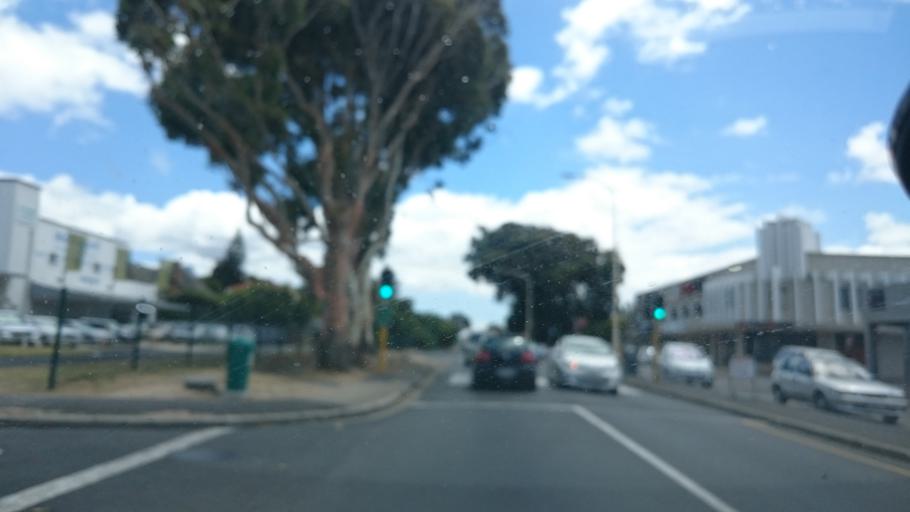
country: ZA
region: Western Cape
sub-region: City of Cape Town
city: Bergvliet
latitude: -34.0450
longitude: 18.4631
